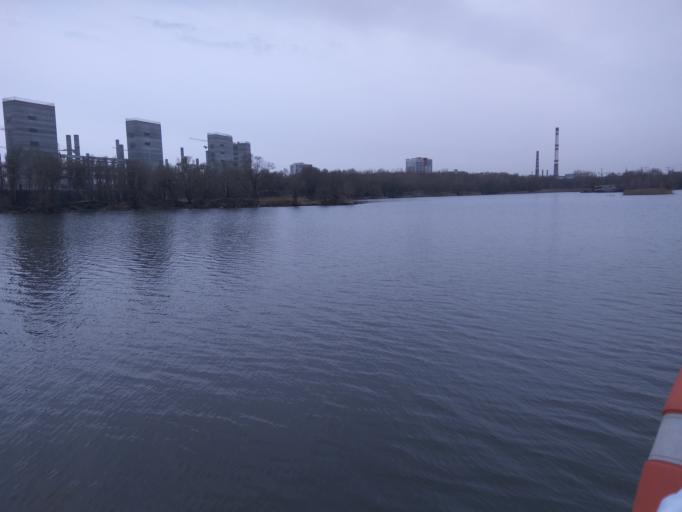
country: RU
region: Moskovskaya
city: Kozhukhovo
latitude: 55.6981
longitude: 37.6817
